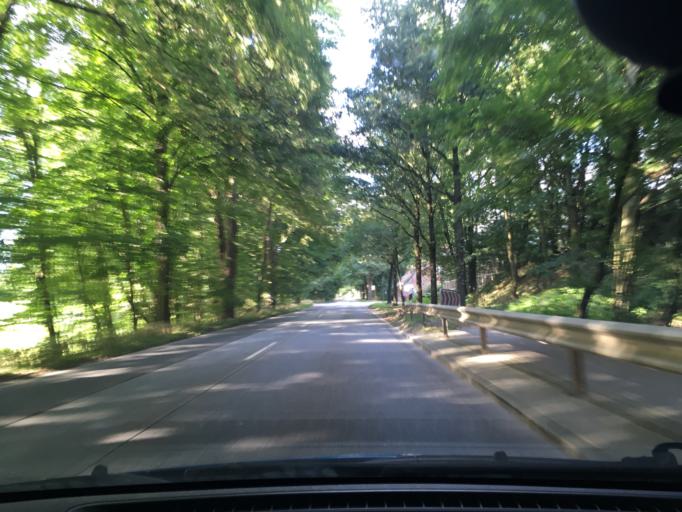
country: DE
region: Lower Saxony
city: Seevetal
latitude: 53.4243
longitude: 9.9305
